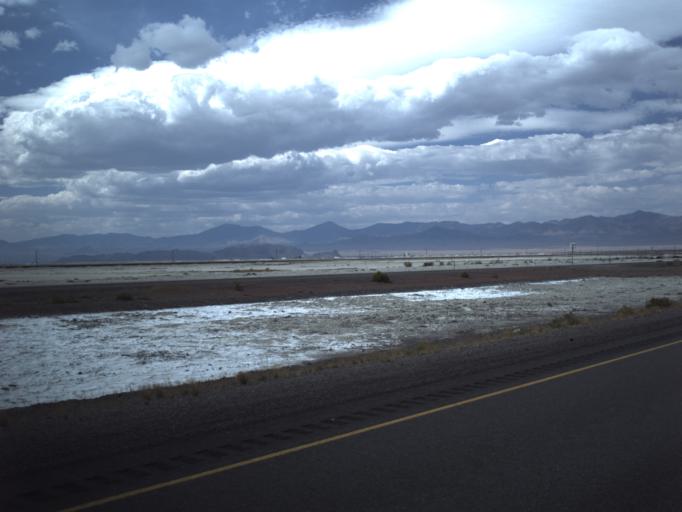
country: US
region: Utah
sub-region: Tooele County
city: Wendover
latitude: 40.7414
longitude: -113.9556
